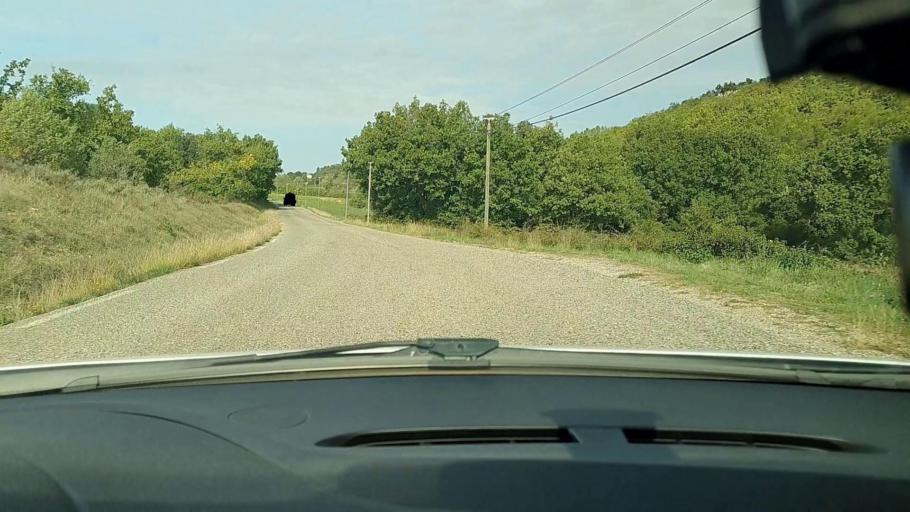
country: FR
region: Languedoc-Roussillon
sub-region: Departement du Gard
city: Goudargues
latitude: 44.1427
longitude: 4.3906
